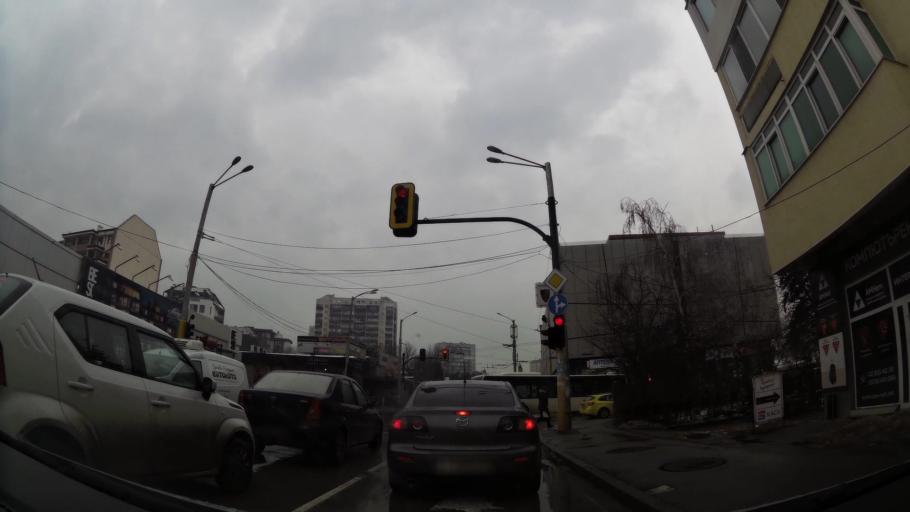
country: BG
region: Sofia-Capital
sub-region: Stolichna Obshtina
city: Sofia
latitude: 42.6683
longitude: 23.2796
